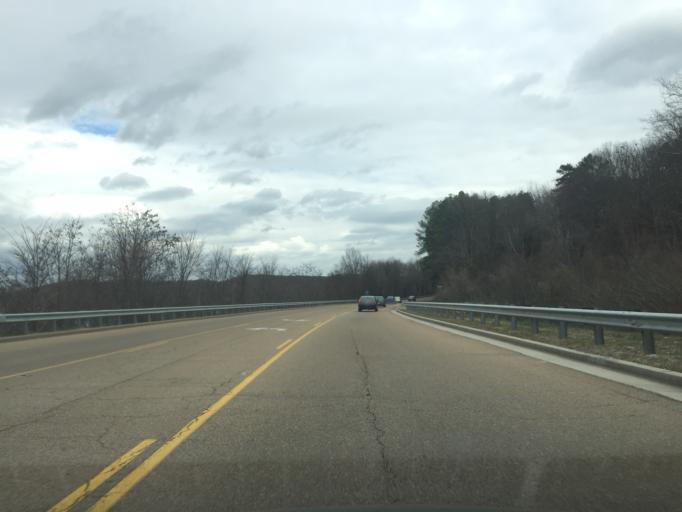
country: US
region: Tennessee
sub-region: Hamilton County
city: Harrison
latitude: 35.0630
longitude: -85.1266
